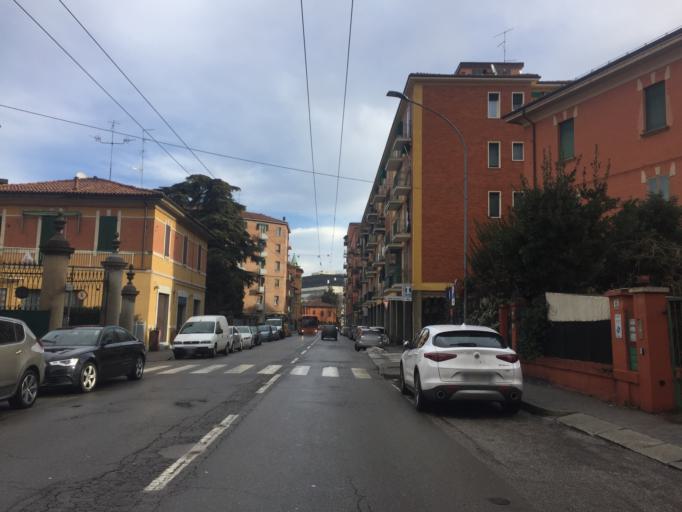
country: IT
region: Emilia-Romagna
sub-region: Provincia di Bologna
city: Bologna
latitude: 44.5061
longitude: 11.3024
